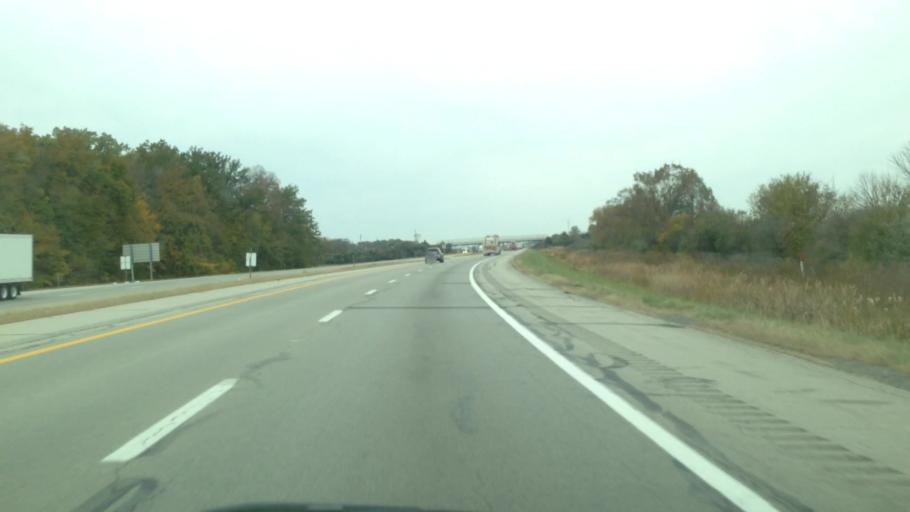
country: US
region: Ohio
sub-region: Fulton County
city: Burlington
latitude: 41.5881
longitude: -84.3460
